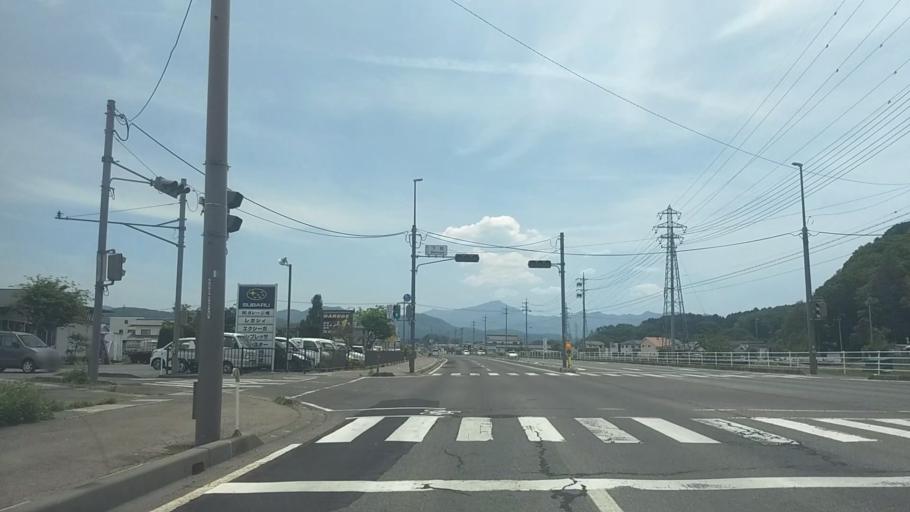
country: JP
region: Nagano
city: Saku
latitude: 36.2017
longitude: 138.4699
